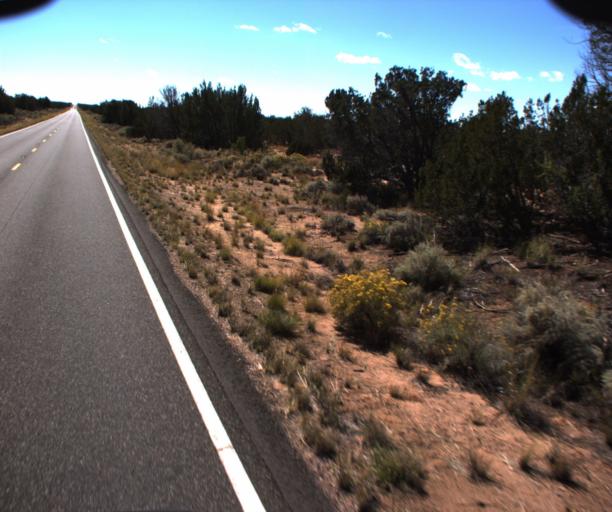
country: US
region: Arizona
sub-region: Apache County
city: Saint Johns
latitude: 34.8681
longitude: -109.2378
